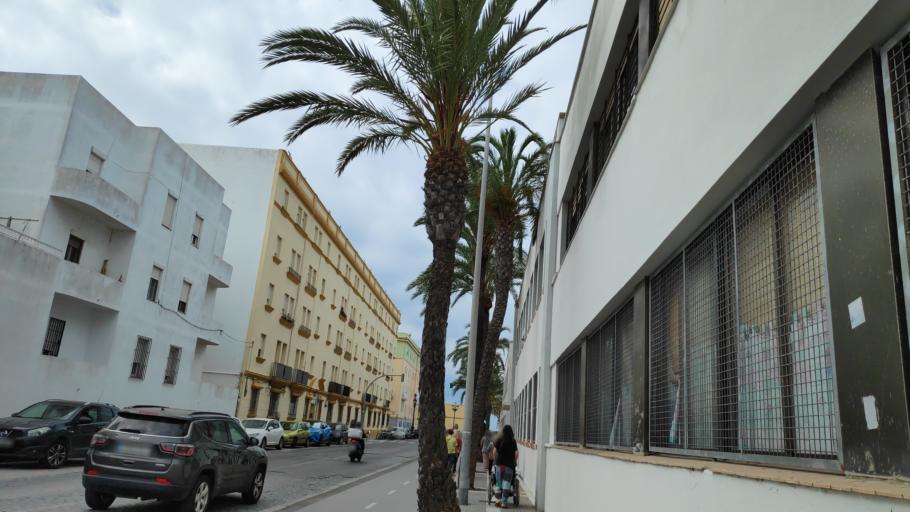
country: ES
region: Andalusia
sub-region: Provincia de Cadiz
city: Cadiz
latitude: 36.5298
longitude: -6.3052
